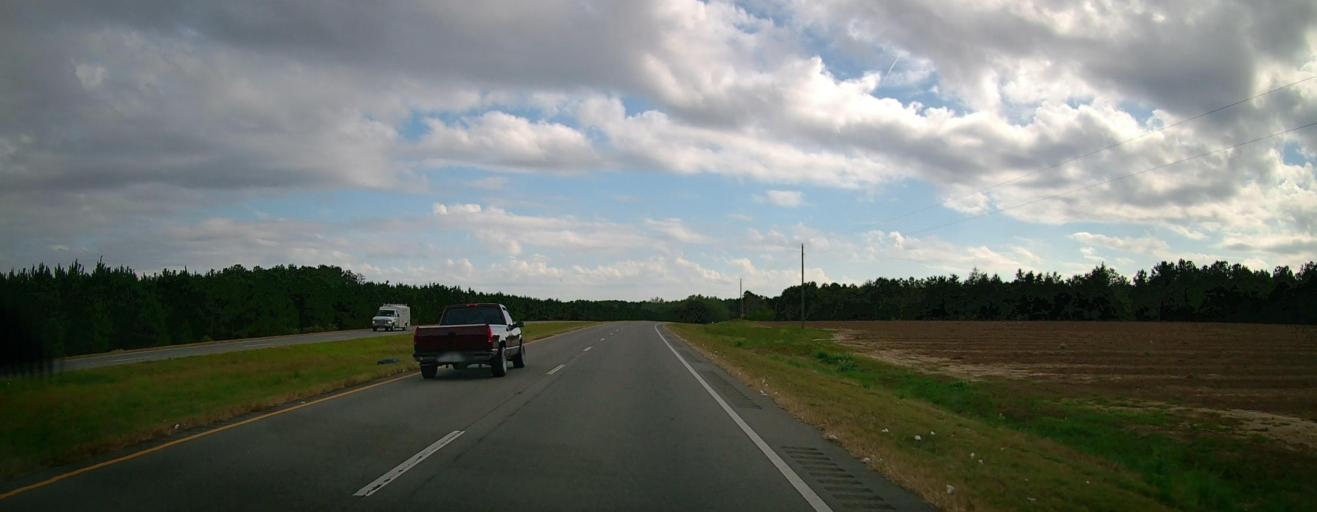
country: US
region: Georgia
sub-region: Thomas County
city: Meigs
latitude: 31.0628
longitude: -84.0735
